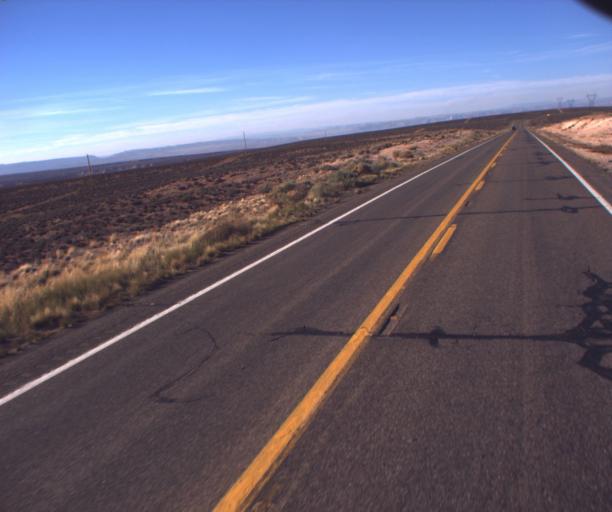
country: US
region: Arizona
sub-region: Coconino County
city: LeChee
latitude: 36.7988
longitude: -111.3016
